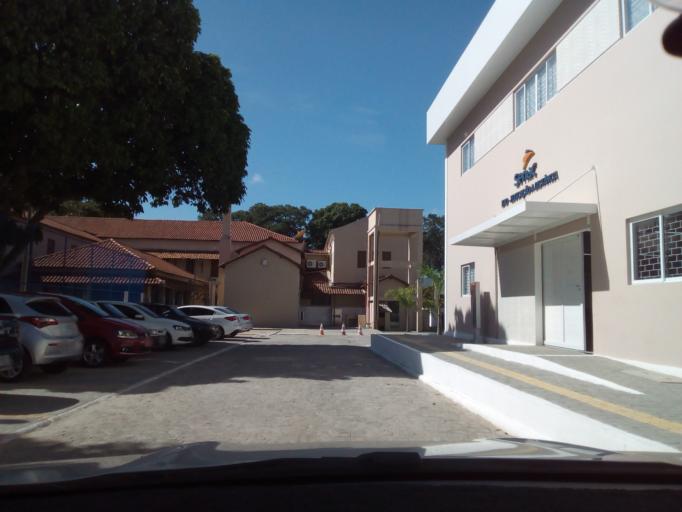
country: BR
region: Paraiba
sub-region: Joao Pessoa
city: Joao Pessoa
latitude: -7.1274
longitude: -34.8724
